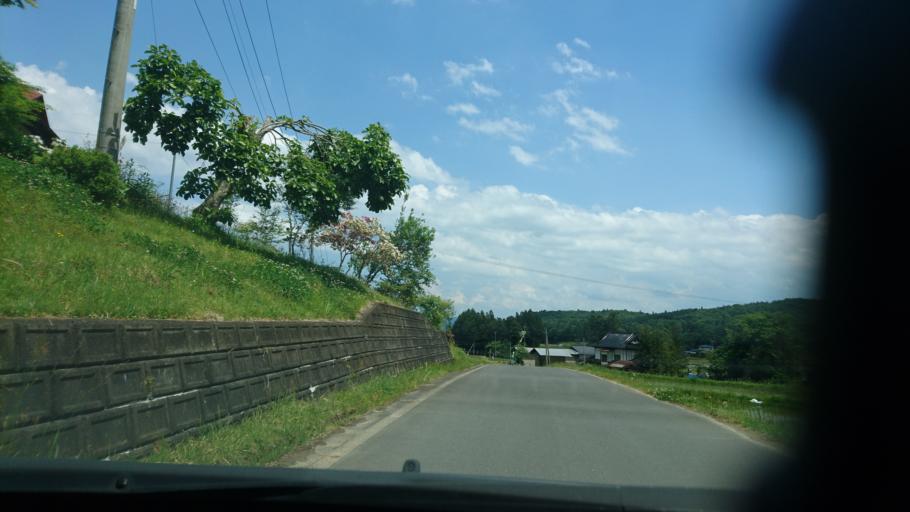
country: JP
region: Iwate
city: Ichinoseki
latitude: 38.9784
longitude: 141.0923
